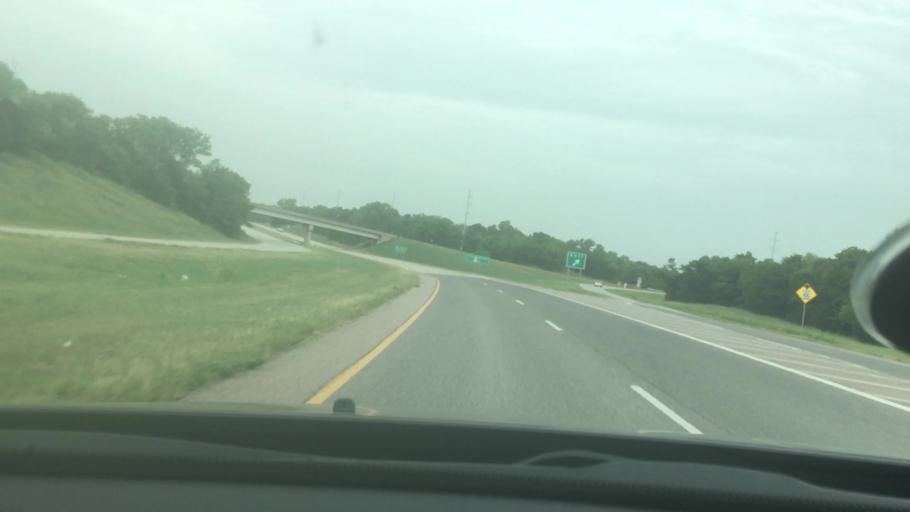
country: US
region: Oklahoma
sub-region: Pontotoc County
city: Ada
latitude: 34.7483
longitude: -96.6543
